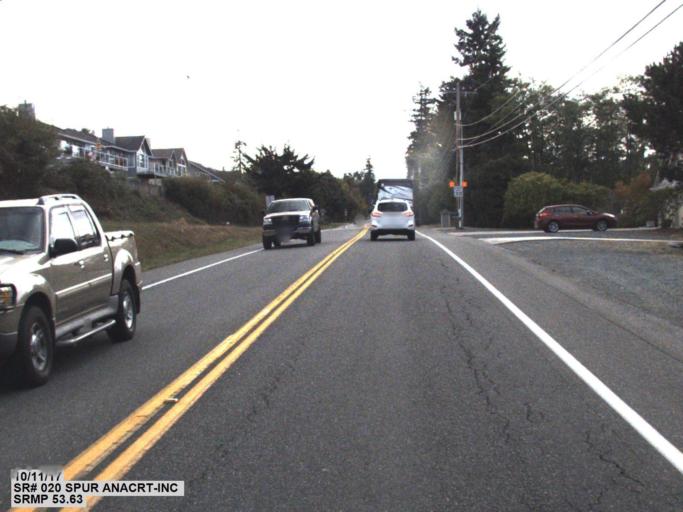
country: US
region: Washington
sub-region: Jefferson County
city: Port Hadlock-Irondale
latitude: 48.0420
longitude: -122.8201
